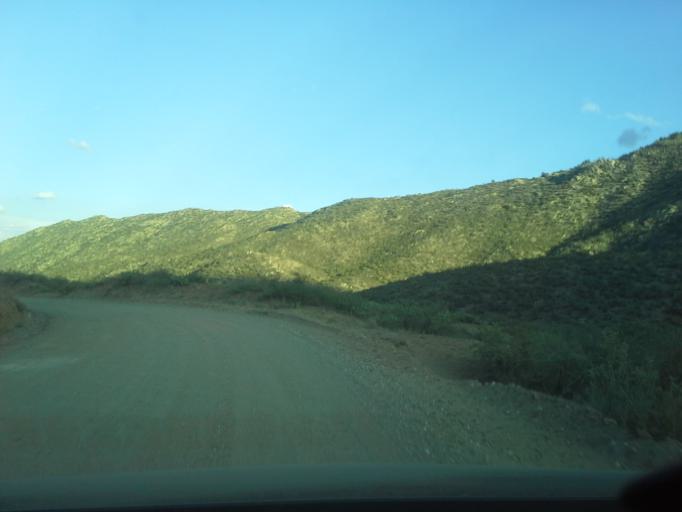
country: US
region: Arizona
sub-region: Yavapai County
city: Mayer
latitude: 34.2748
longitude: -112.2762
